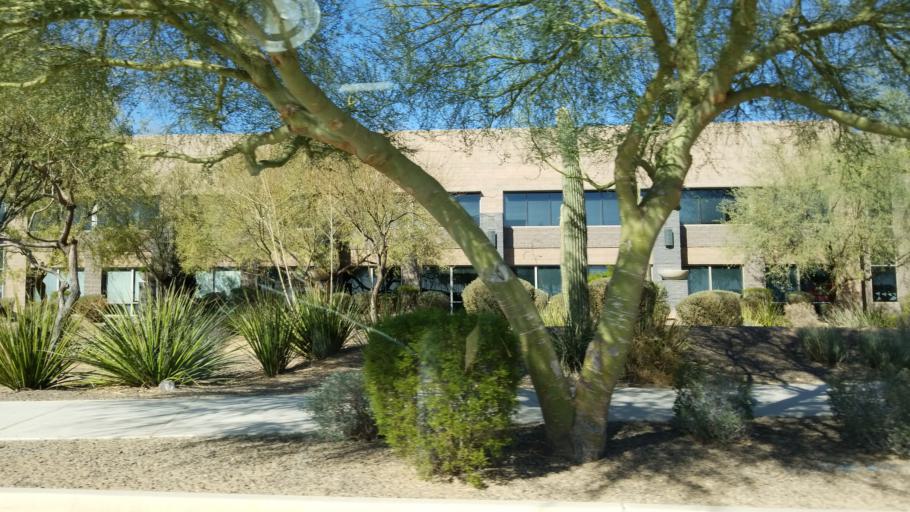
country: US
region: Arizona
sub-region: Maricopa County
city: Scottsdale
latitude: 33.5536
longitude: -111.8841
